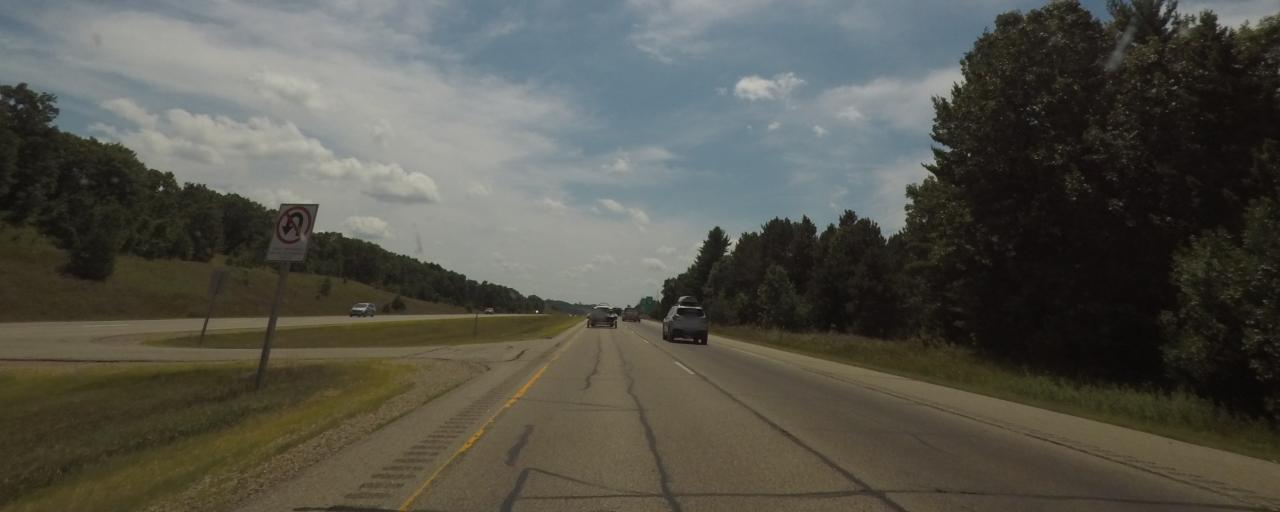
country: US
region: Wisconsin
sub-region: Marquette County
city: Westfield
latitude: 43.8115
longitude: -89.4827
